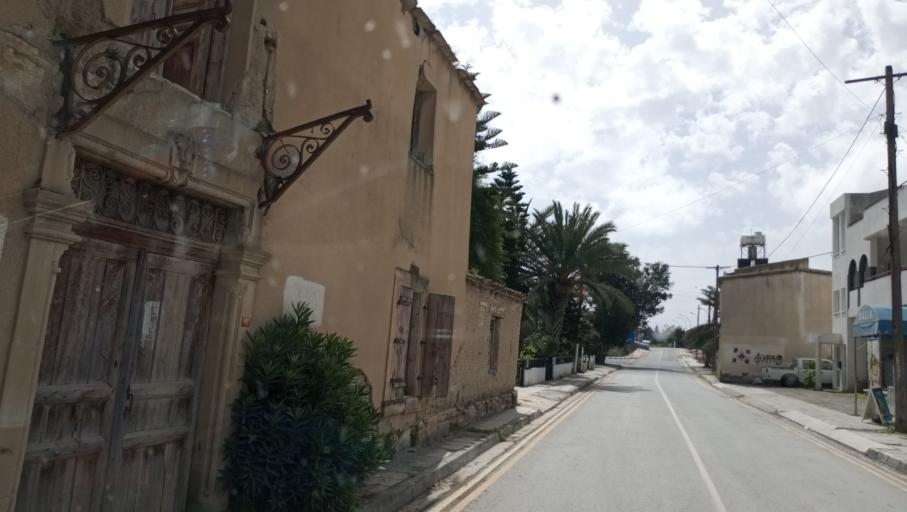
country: CY
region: Lefkosia
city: Dali
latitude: 35.0214
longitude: 33.4233
